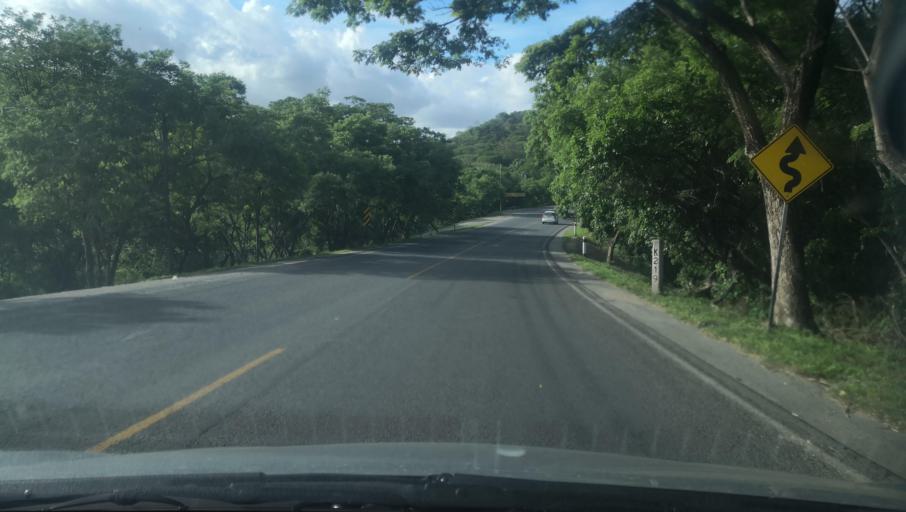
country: NI
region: Madriz
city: Totogalpa
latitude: 13.5838
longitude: -86.4782
